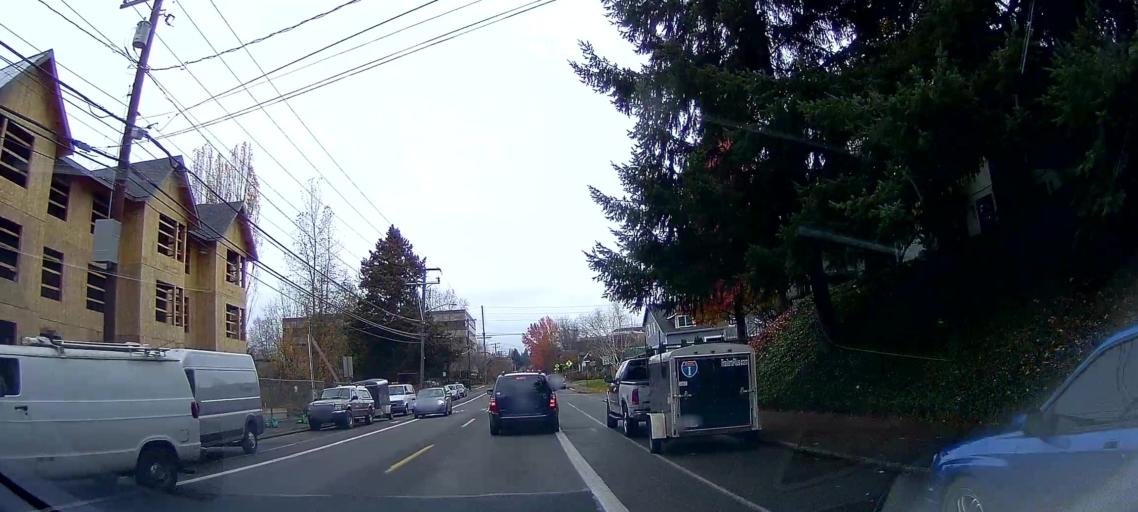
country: US
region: Washington
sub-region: Thurston County
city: Olympia
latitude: 47.0412
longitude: -122.8878
